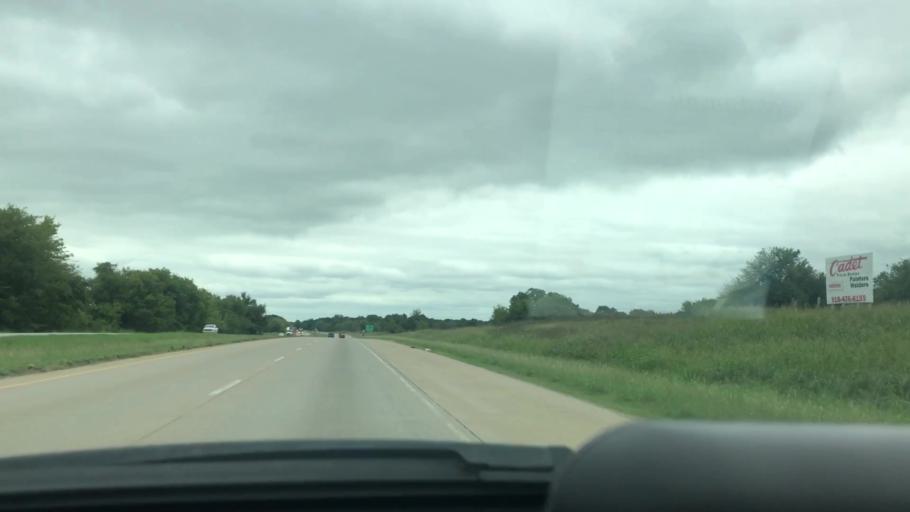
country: US
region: Oklahoma
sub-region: Mayes County
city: Chouteau
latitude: 36.1954
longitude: -95.3415
